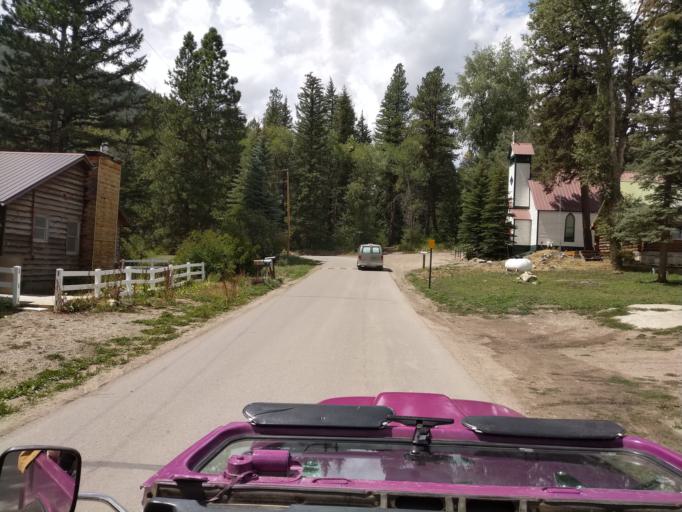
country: US
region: Colorado
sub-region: Gunnison County
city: Crested Butte
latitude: 39.0710
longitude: -107.1887
